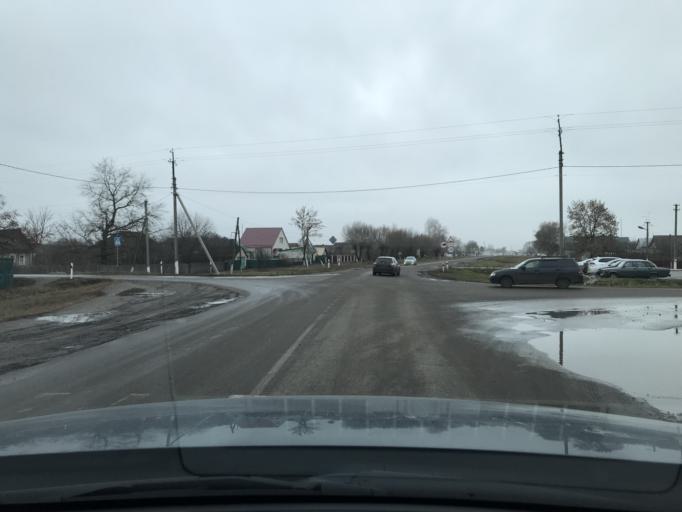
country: RU
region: Penza
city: Zemetchino
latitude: 53.5007
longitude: 42.6302
